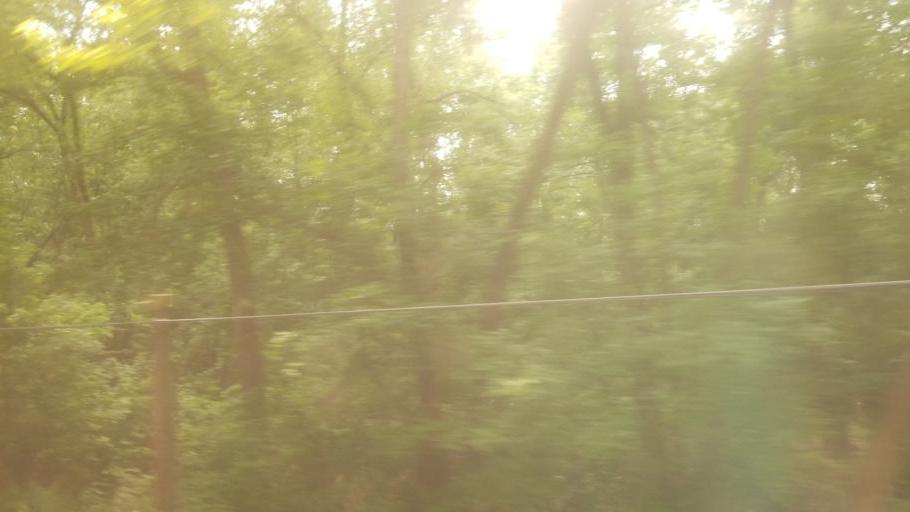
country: US
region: Maryland
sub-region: Frederick County
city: Point of Rocks
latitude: 39.2815
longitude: -77.5474
